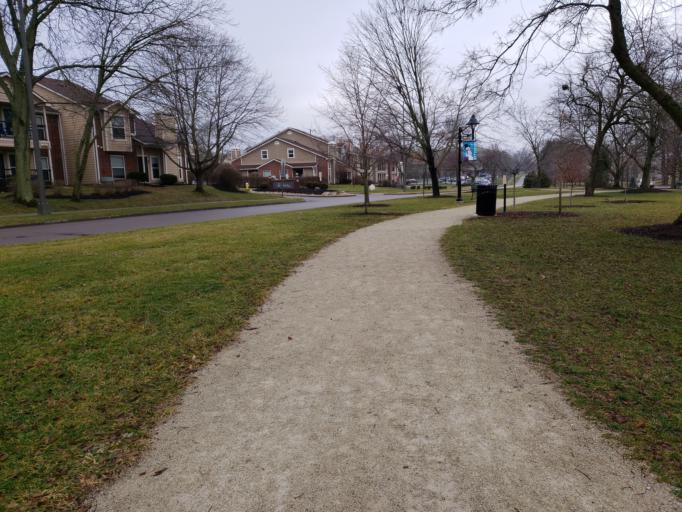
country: US
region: Ohio
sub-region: Montgomery County
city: Kettering
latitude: 39.6966
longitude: -84.1558
